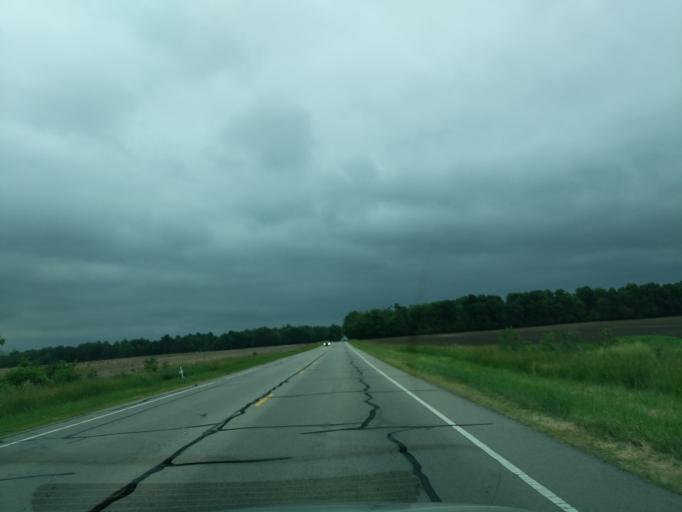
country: US
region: Indiana
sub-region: Madison County
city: Alexandria
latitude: 40.2773
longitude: -85.6098
